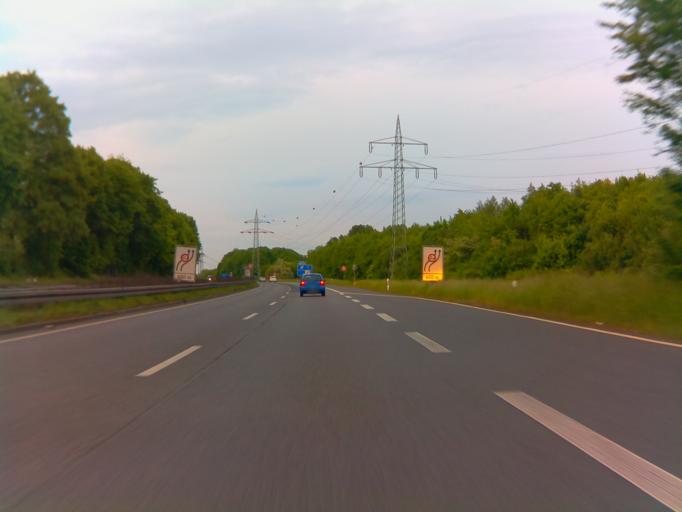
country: DE
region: Hesse
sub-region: Regierungsbezirk Kassel
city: Baunatal
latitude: 51.2459
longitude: 9.4356
